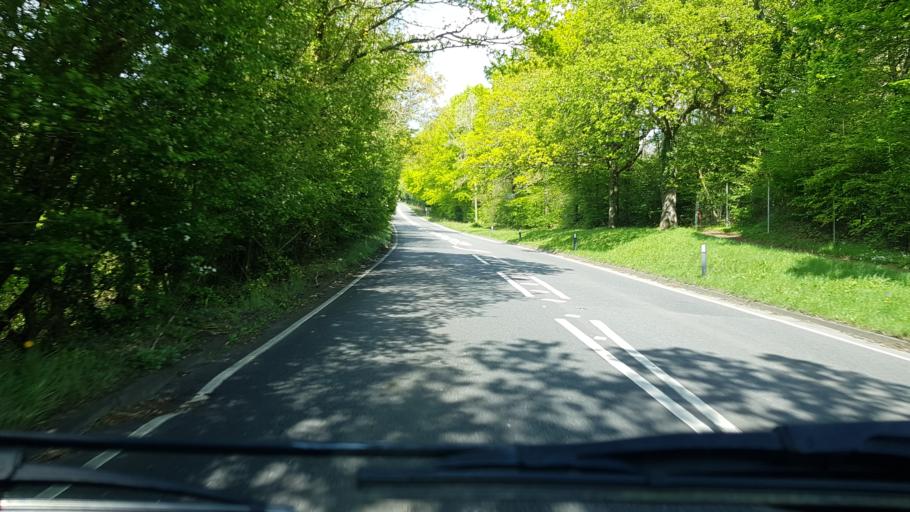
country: GB
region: England
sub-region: Kent
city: Hawkhurst
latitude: 51.0471
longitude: 0.4471
